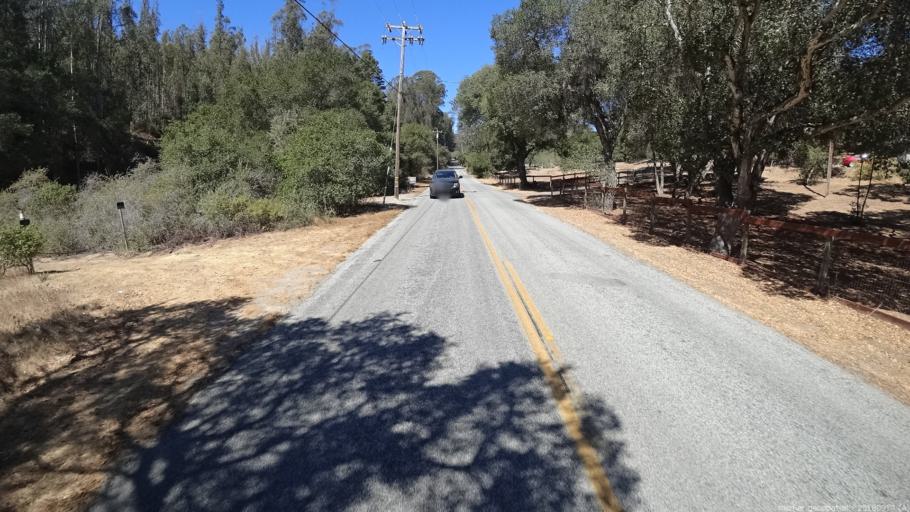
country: US
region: California
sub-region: Monterey County
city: Las Lomas
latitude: 36.8800
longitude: -121.6939
